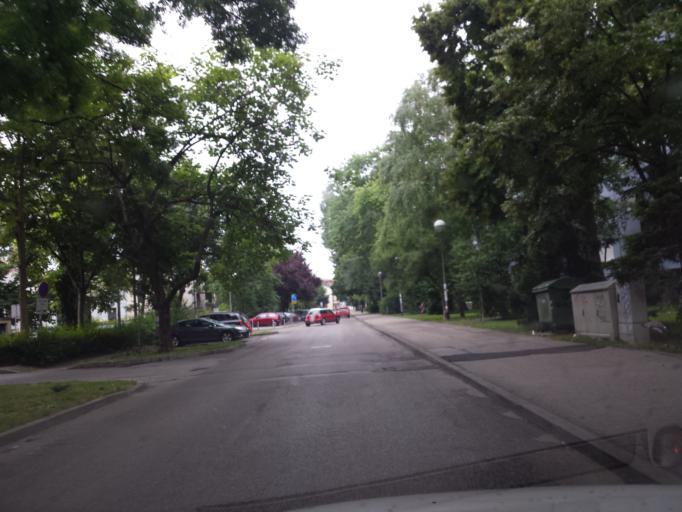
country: HR
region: Grad Zagreb
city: Zagreb - Centar
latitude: 45.7988
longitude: 15.9680
